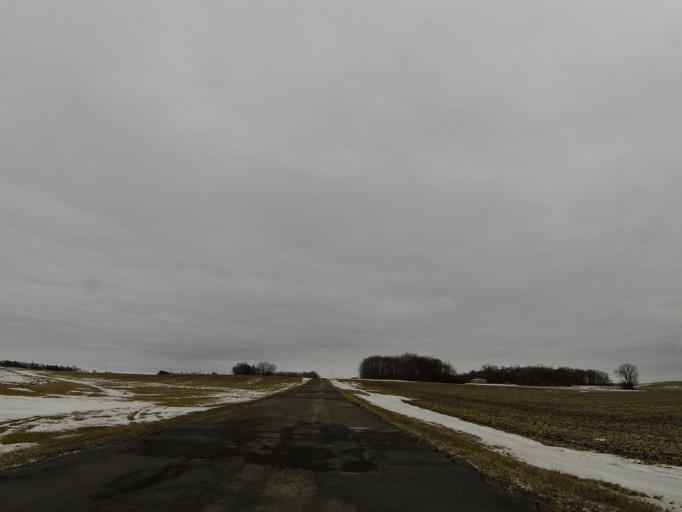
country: US
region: Minnesota
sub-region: Washington County
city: Cottage Grove
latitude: 44.8047
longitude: -92.8822
